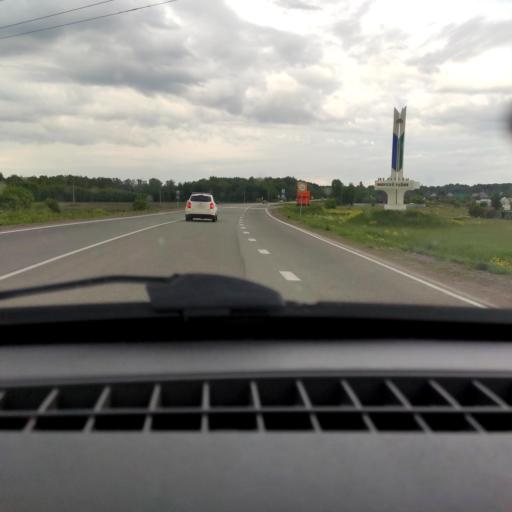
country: RU
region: Bashkortostan
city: Avdon
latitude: 54.5723
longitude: 55.6979
